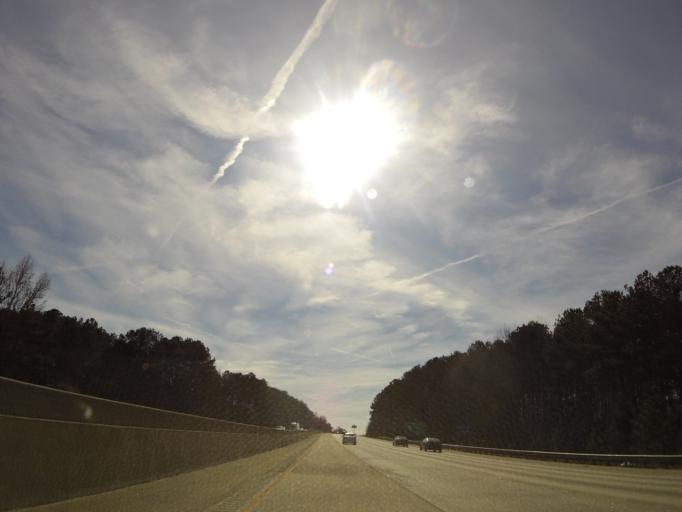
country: US
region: Georgia
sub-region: Coweta County
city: Newnan
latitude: 33.4112
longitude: -84.7355
